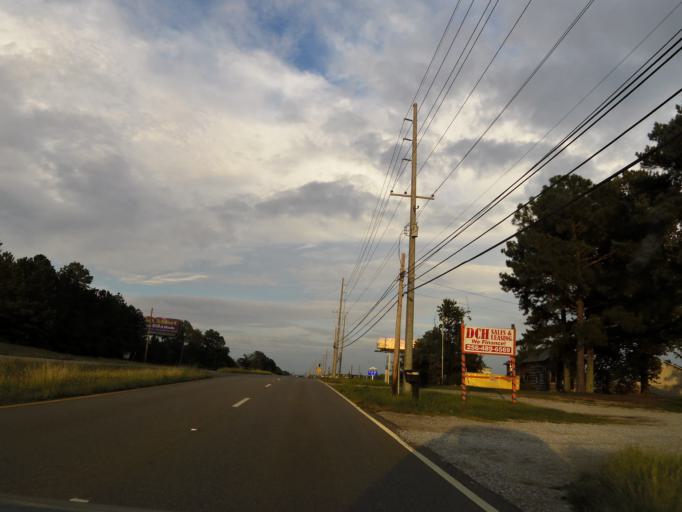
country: US
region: Alabama
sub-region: Madison County
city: Madison
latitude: 34.7480
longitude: -86.7716
